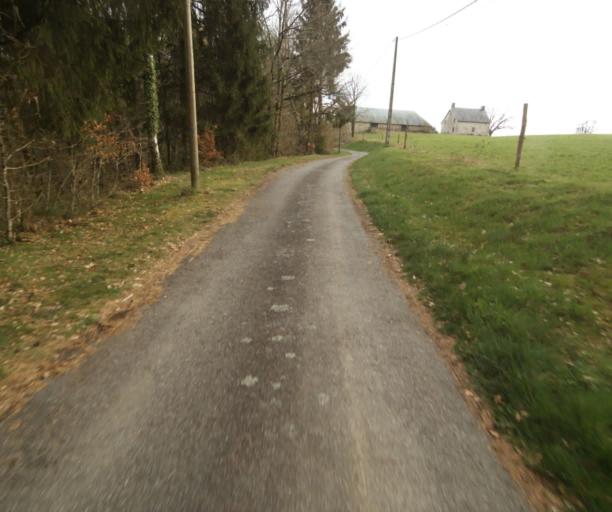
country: FR
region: Limousin
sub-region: Departement de la Correze
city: Argentat
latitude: 45.2059
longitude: 1.9908
